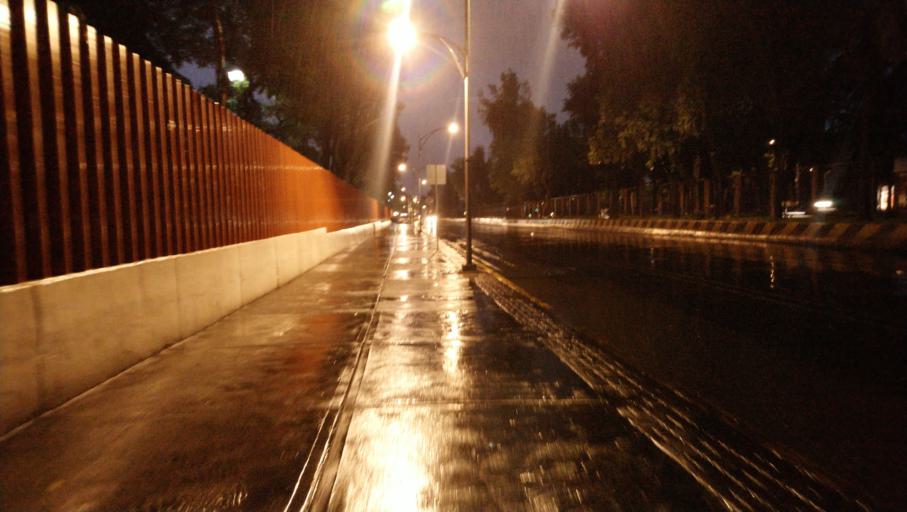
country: MX
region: Mexico City
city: Mexico City
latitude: 19.4320
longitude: -99.1188
